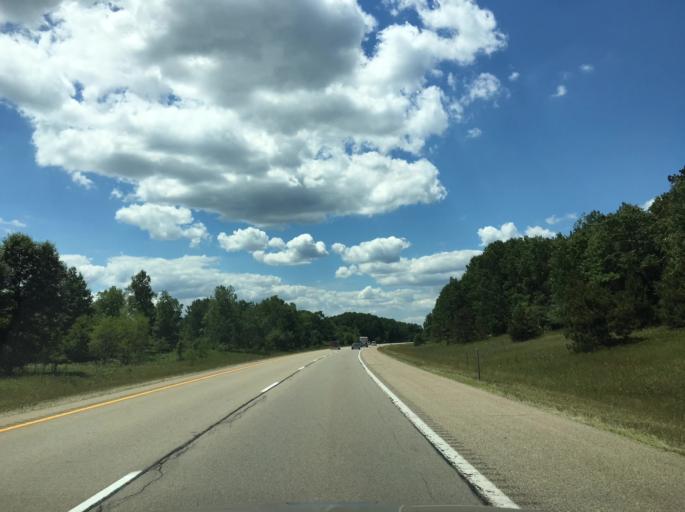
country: US
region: Michigan
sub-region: Clare County
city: Clare
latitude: 43.8765
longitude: -84.8204
